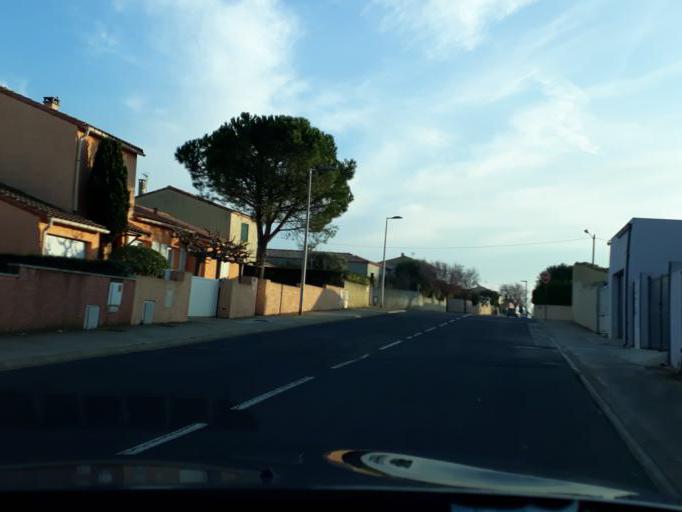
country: FR
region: Languedoc-Roussillon
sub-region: Departement de l'Herault
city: Marseillan
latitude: 43.3499
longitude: 3.5297
